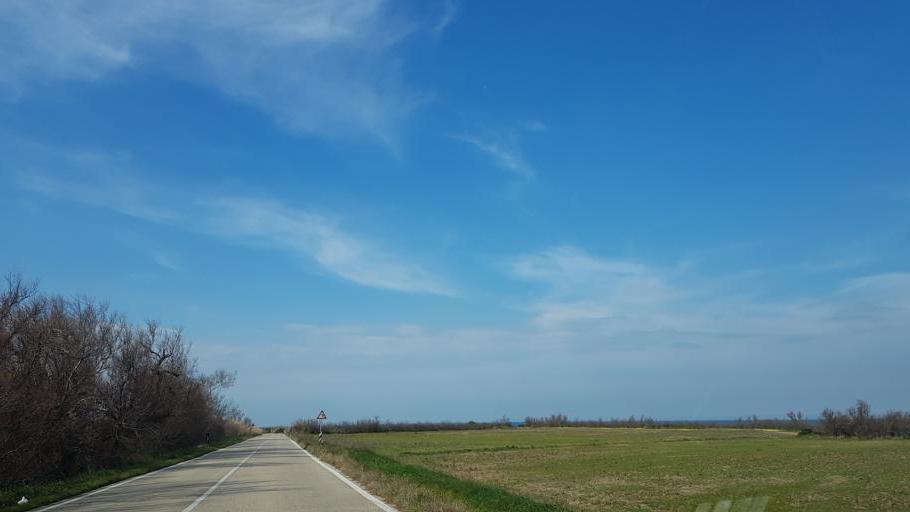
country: IT
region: Apulia
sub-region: Provincia di Brindisi
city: Brindisi
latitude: 40.6856
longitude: 17.8608
